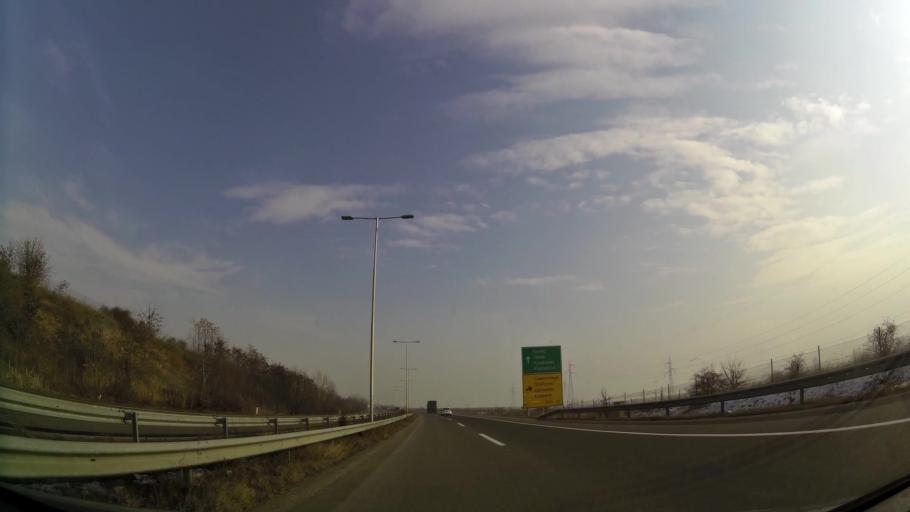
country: MK
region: Butel
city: Butel
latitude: 42.0328
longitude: 21.4769
